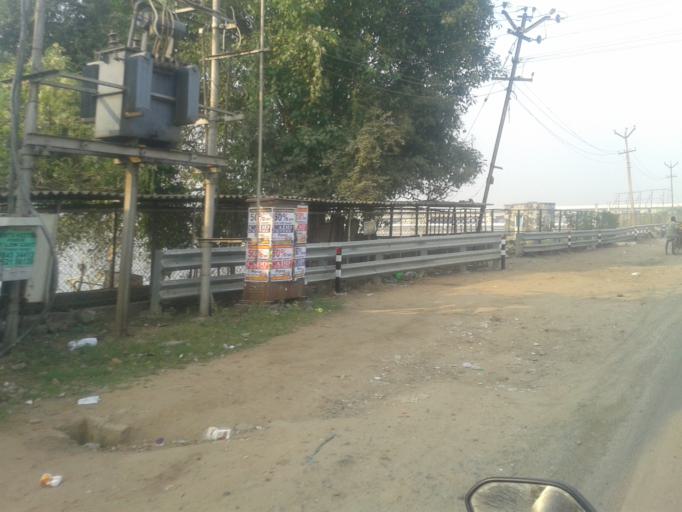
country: IN
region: Tamil Nadu
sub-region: Thiruvallur
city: Porur
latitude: 13.0362
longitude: 80.1518
